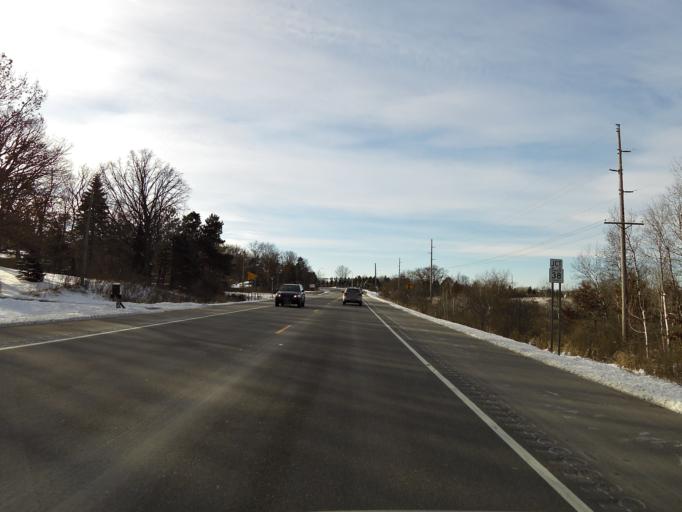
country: US
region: Minnesota
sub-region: Dakota County
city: Rosemount
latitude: 44.7703
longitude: -93.1200
